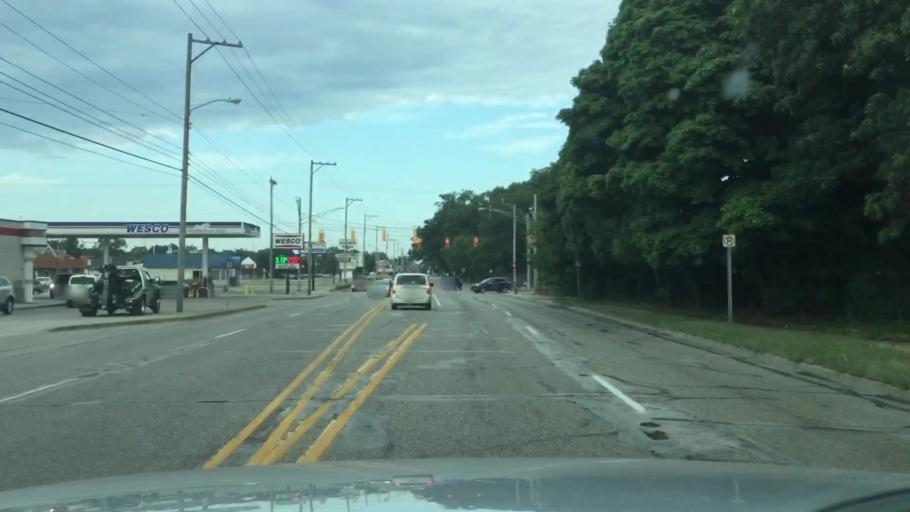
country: US
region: Michigan
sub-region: Muskegon County
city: Roosevelt Park
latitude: 43.2056
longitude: -86.2769
